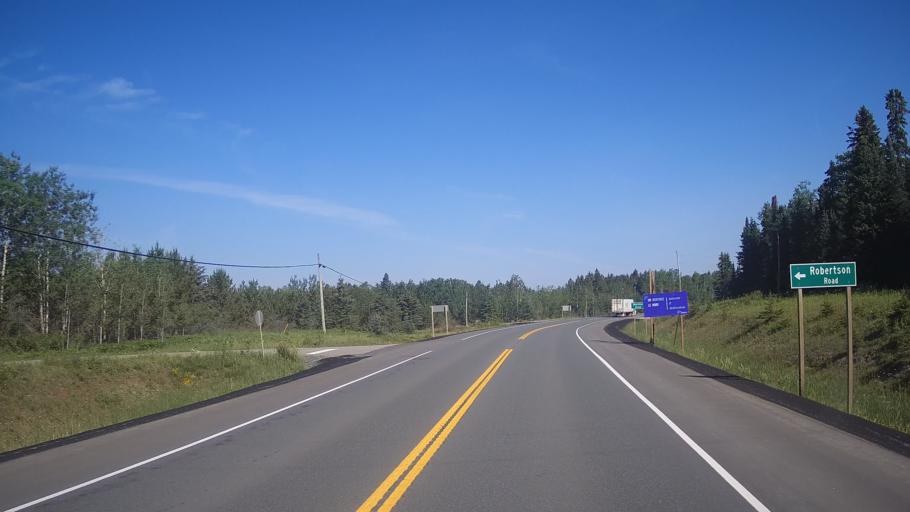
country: CA
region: Ontario
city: Dryden
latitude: 49.6684
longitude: -92.4903
